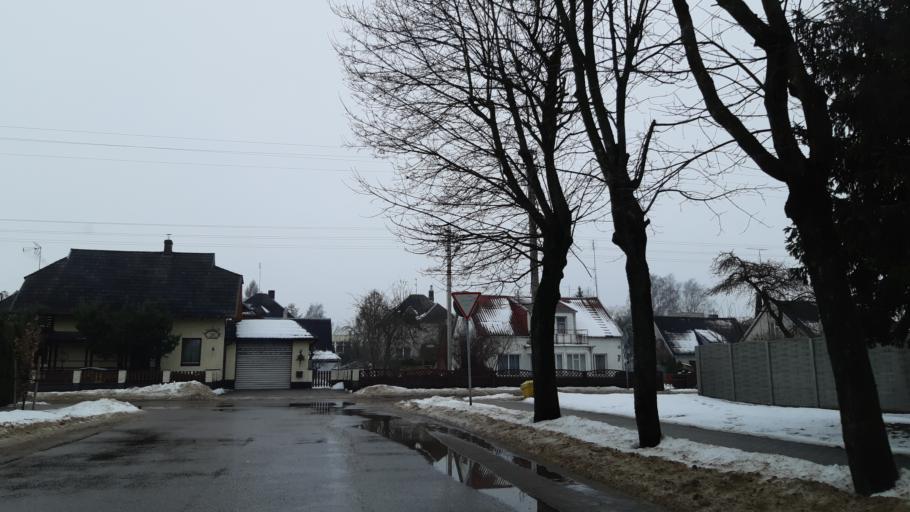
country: LT
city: Vilkaviskis
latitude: 54.6466
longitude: 23.0346
